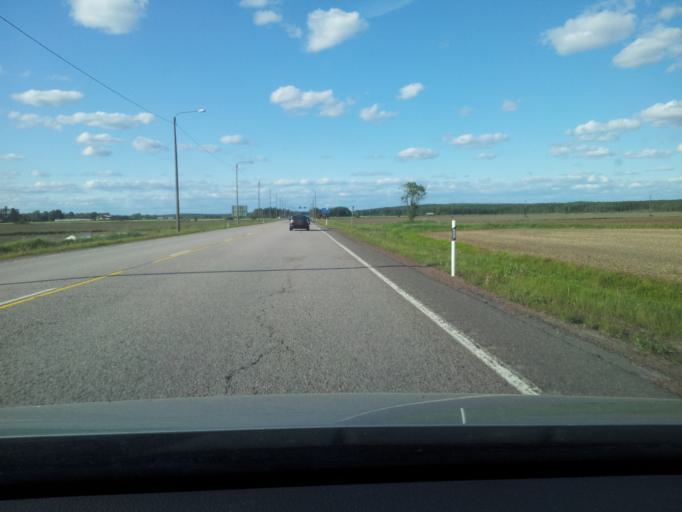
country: FI
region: Uusimaa
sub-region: Loviisa
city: Lapinjaervi
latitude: 60.6517
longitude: 26.2378
